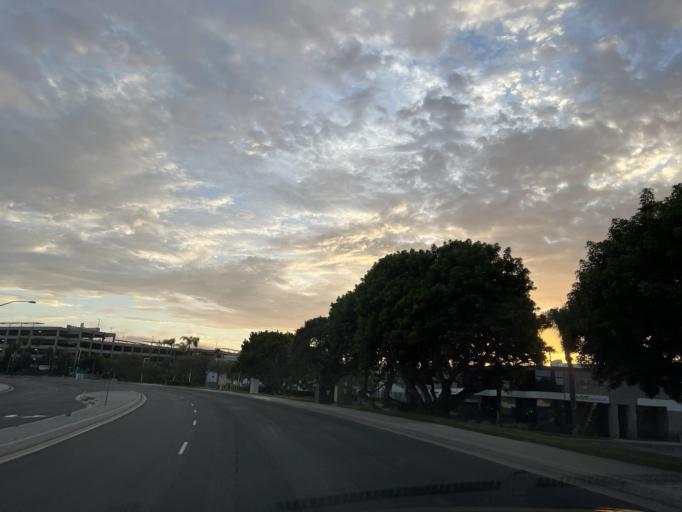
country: US
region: California
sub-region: San Diego County
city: Del Mar
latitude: 32.9042
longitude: -117.1973
